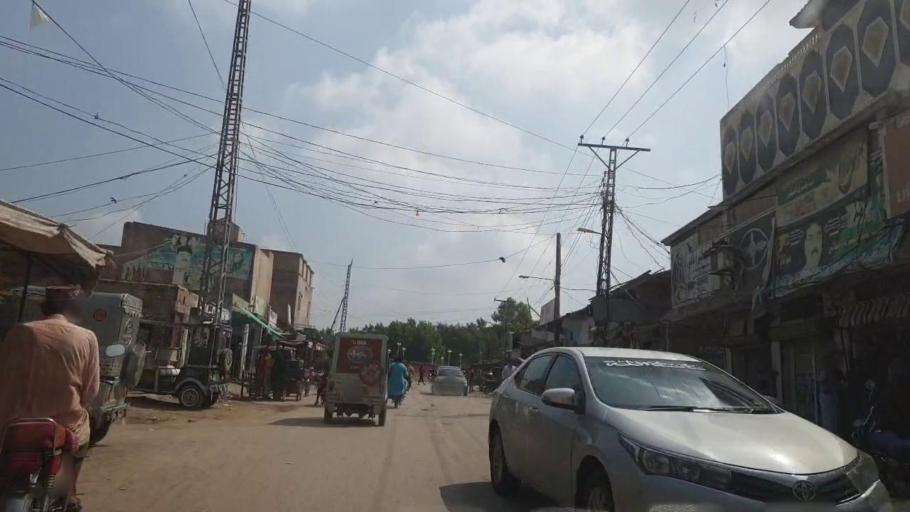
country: PK
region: Sindh
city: Khairpur
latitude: 27.5353
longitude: 68.7517
